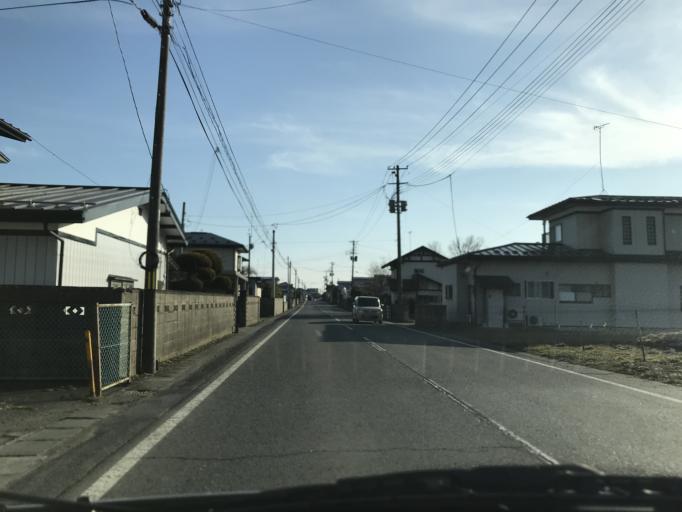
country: JP
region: Iwate
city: Kitakami
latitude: 39.2678
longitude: 141.1169
